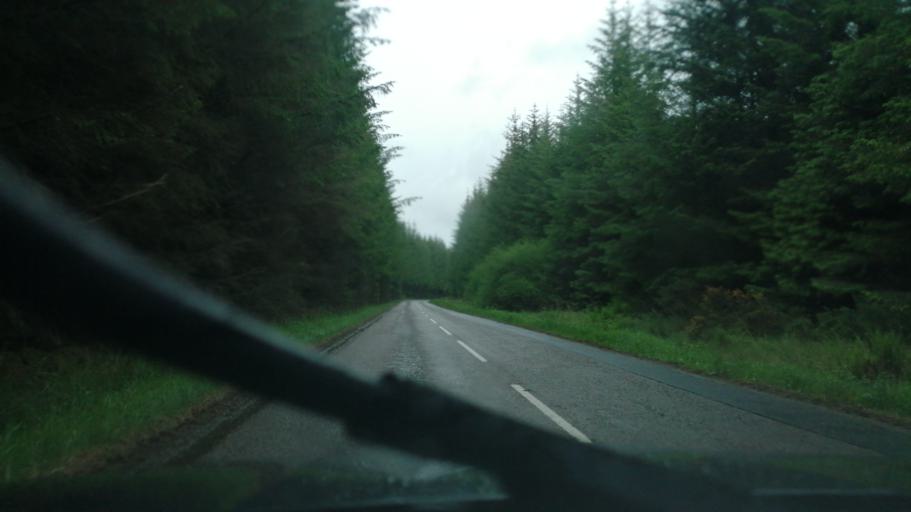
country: GB
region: Scotland
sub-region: Aberdeenshire
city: Portsoy
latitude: 57.6320
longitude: -2.7176
